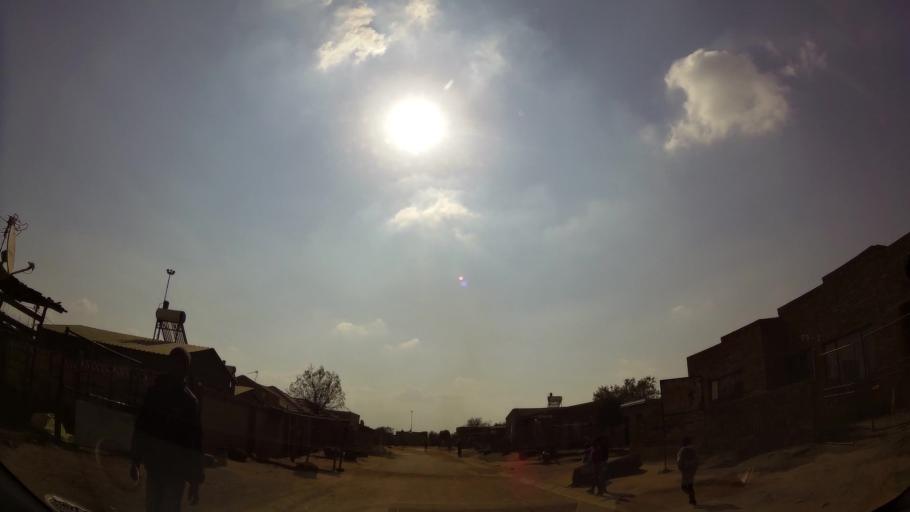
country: ZA
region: Gauteng
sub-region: Ekurhuleni Metropolitan Municipality
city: Springs
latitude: -26.1163
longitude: 28.4835
